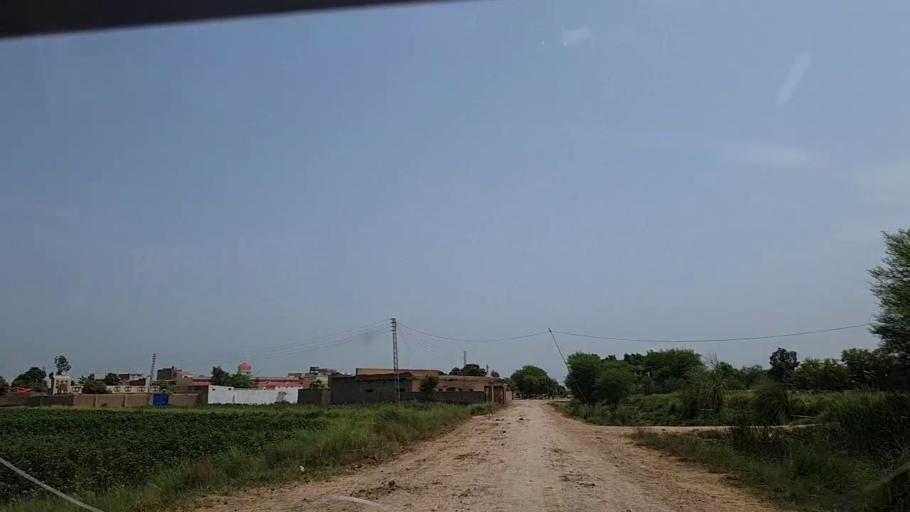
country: PK
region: Sindh
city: Tharu Shah
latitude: 26.8970
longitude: 68.0480
